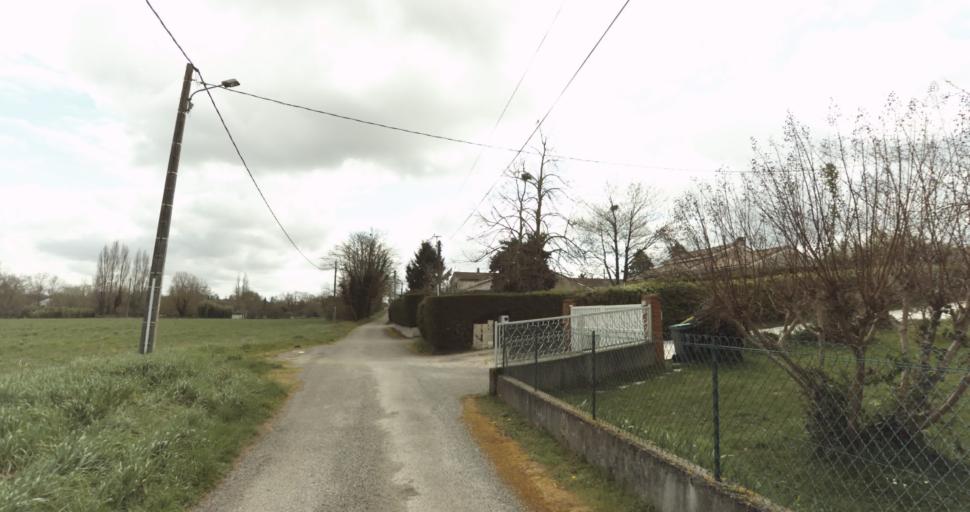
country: FR
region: Midi-Pyrenees
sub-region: Departement de la Haute-Garonne
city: Auterive
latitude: 43.3567
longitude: 1.4696
